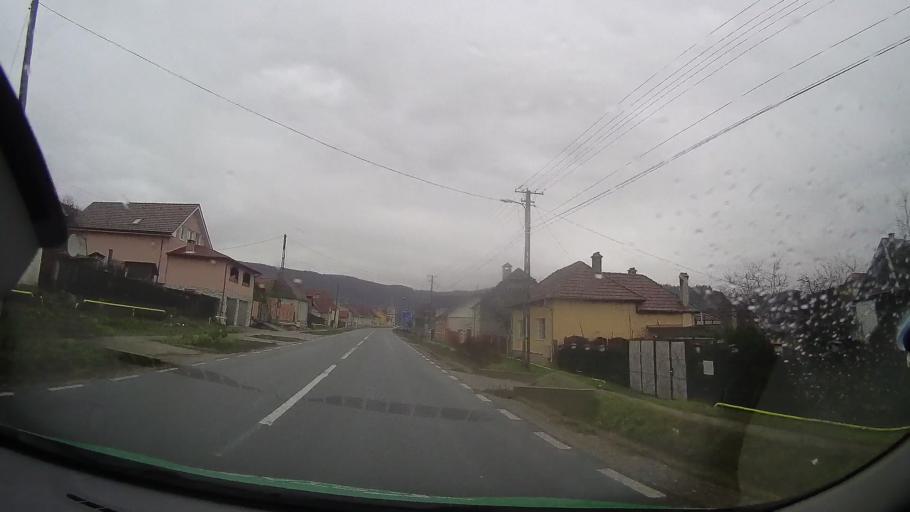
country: RO
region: Bistrita-Nasaud
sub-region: Comuna Teaca
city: Teaca
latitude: 46.9131
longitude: 24.5002
